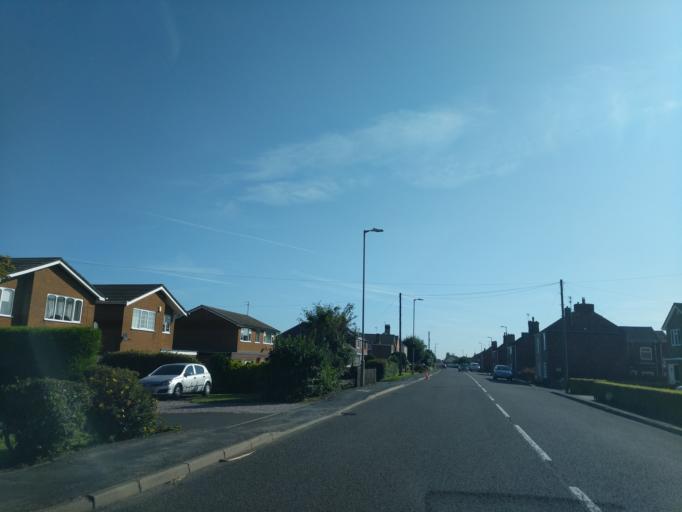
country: GB
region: England
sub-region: Lincolnshire
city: Spalding
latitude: 52.7830
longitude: -0.1736
